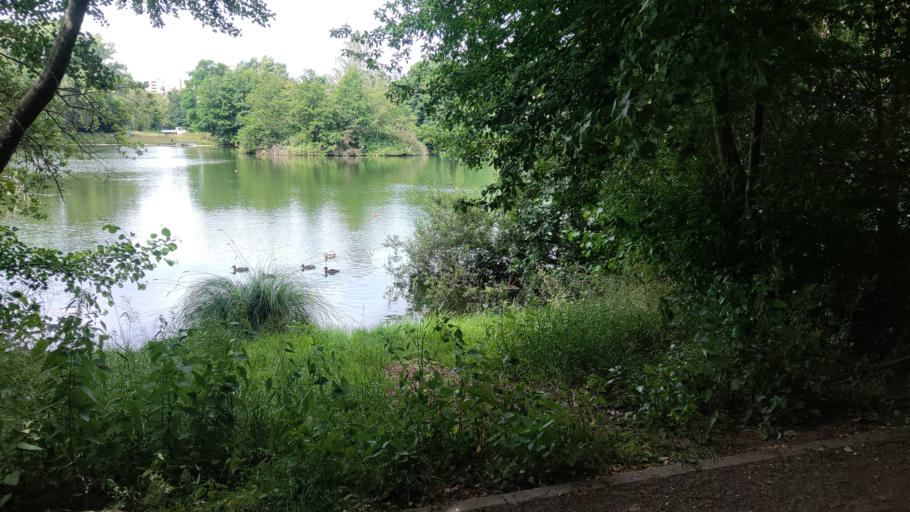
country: DE
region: Berlin
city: Lubars
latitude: 52.6104
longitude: 13.3462
